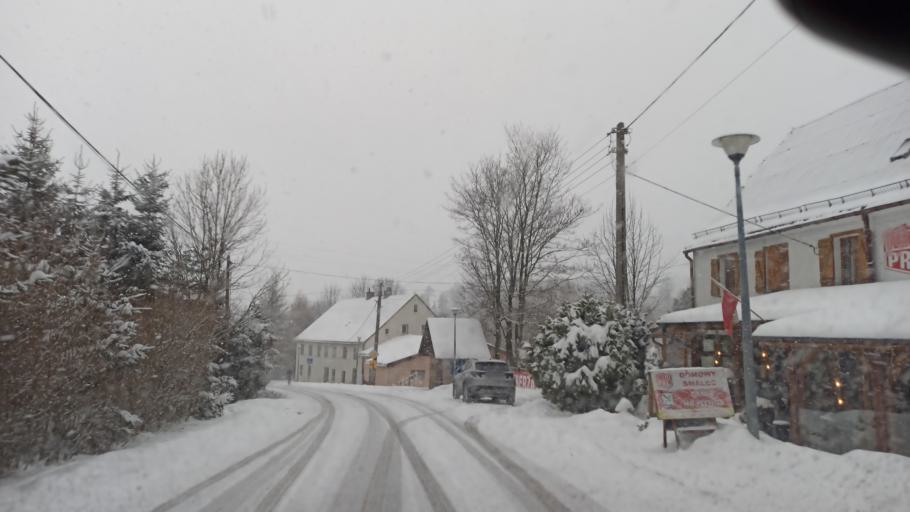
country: PL
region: Lower Silesian Voivodeship
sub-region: Powiat klodzki
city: Ludwikowice Klodzkie
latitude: 50.6536
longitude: 16.4725
